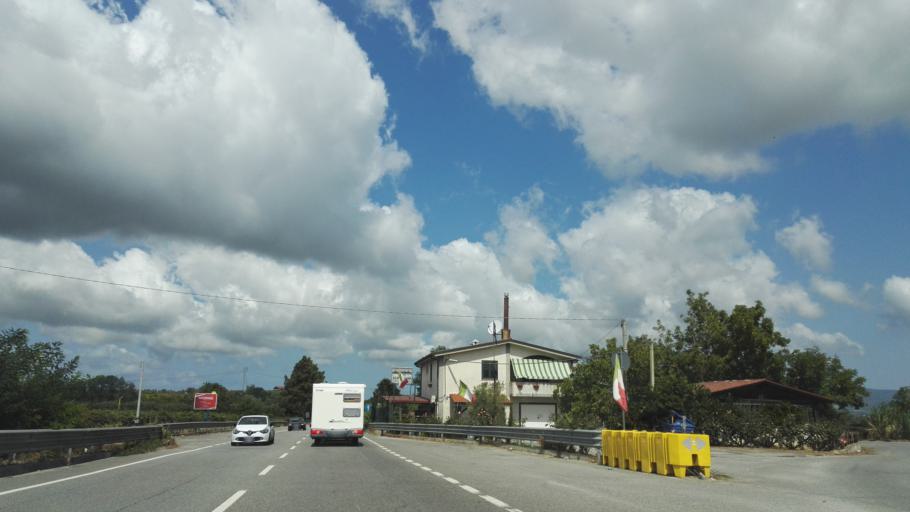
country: IT
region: Calabria
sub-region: Provincia di Reggio Calabria
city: Melicucco
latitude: 38.4578
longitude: 16.0215
